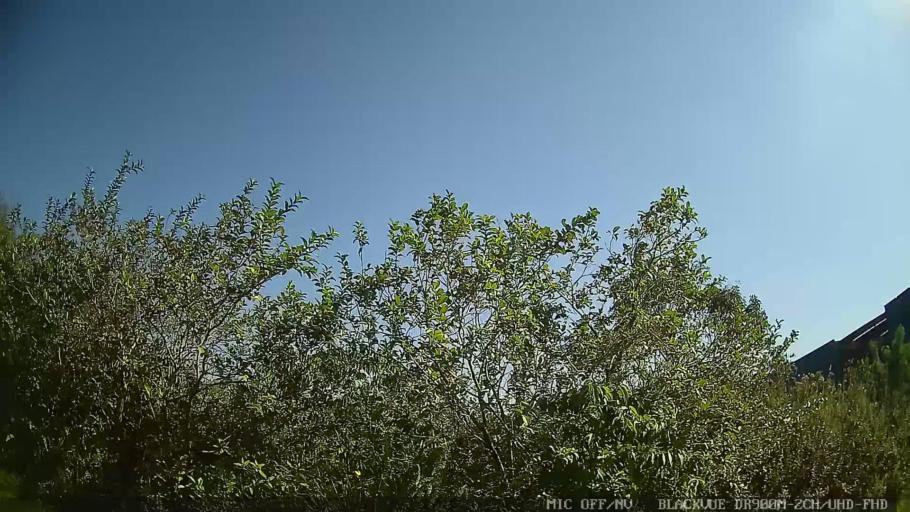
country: BR
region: Sao Paulo
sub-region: Guaruja
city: Guaruja
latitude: -24.0051
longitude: -46.2908
